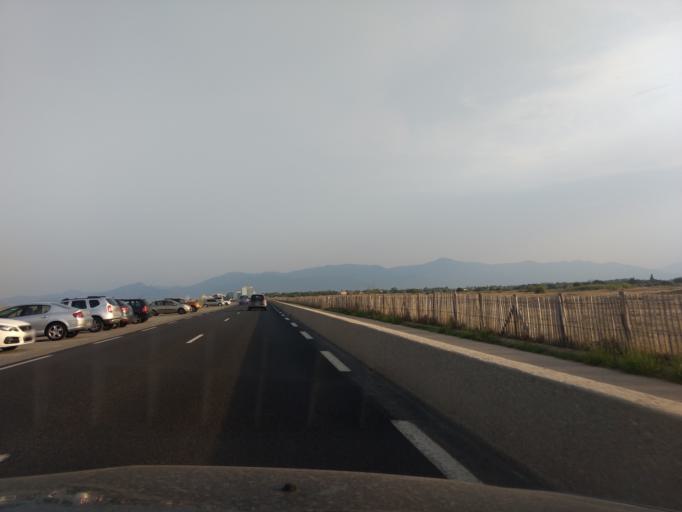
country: FR
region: Languedoc-Roussillon
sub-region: Departement des Pyrenees-Orientales
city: Saint-Cyprien-Plage
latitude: 42.6513
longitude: 3.0331
